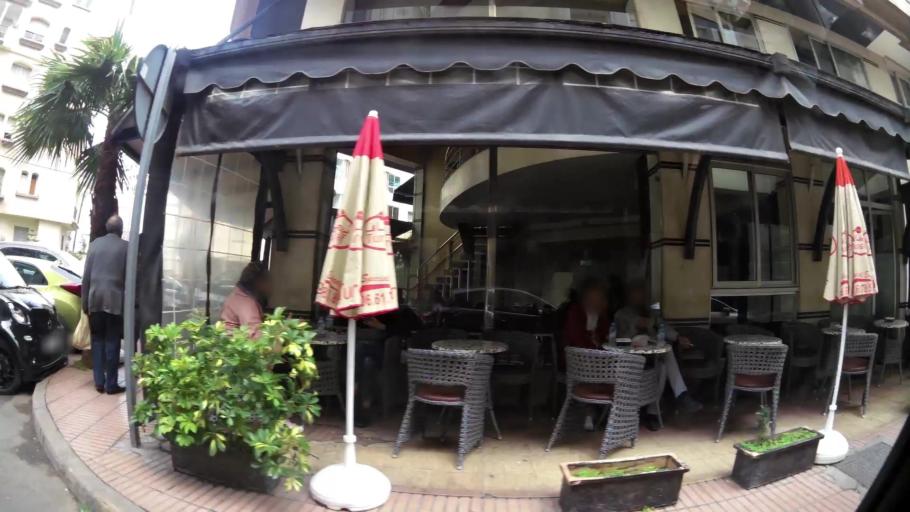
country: MA
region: Grand Casablanca
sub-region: Casablanca
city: Casablanca
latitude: 33.5905
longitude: -7.6343
